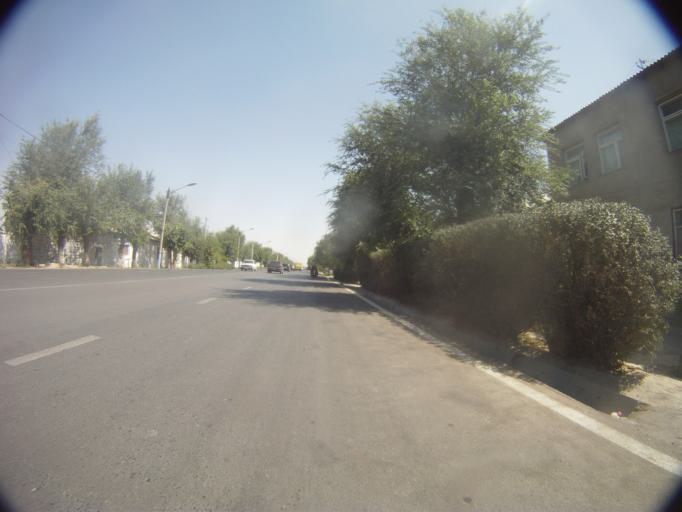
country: KZ
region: Ongtustik Qazaqstan
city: Turkestan
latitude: 43.3012
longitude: 68.2583
